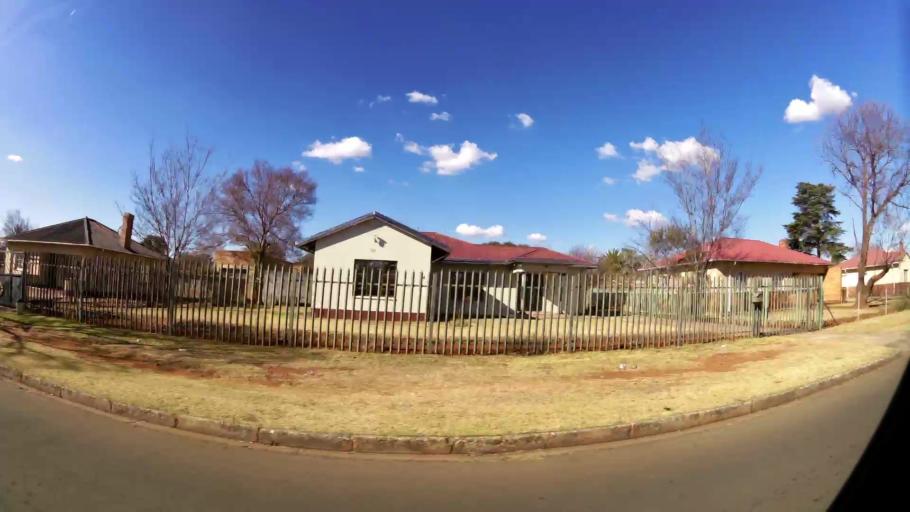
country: ZA
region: Gauteng
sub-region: West Rand District Municipality
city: Carletonville
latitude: -26.3656
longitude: 27.3940
